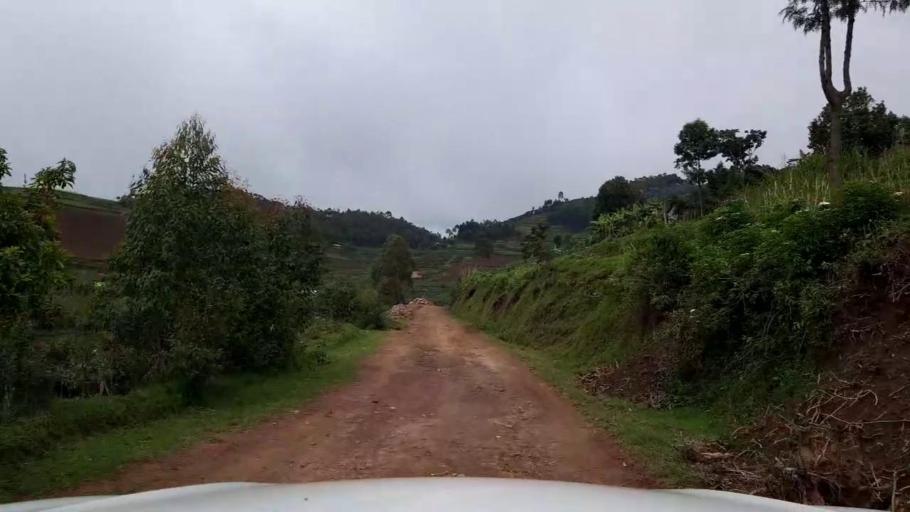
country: RW
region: Northern Province
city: Musanze
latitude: -1.6051
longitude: 29.7673
